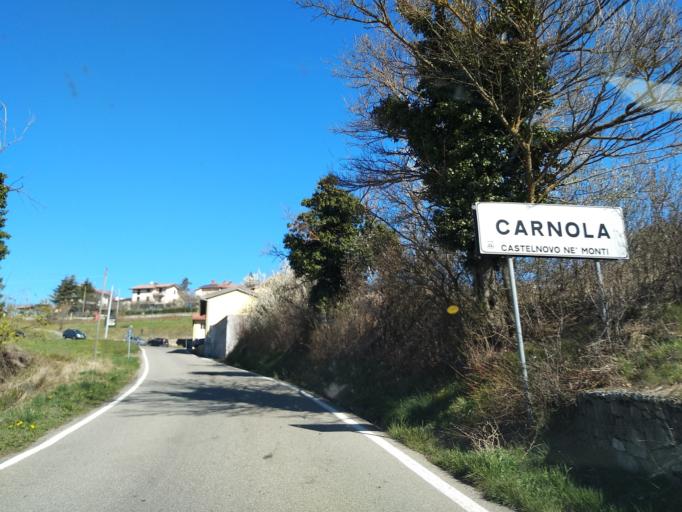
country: IT
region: Emilia-Romagna
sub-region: Provincia di Reggio Emilia
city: Castelnovo ne'Monti
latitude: 44.4132
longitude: 10.4025
